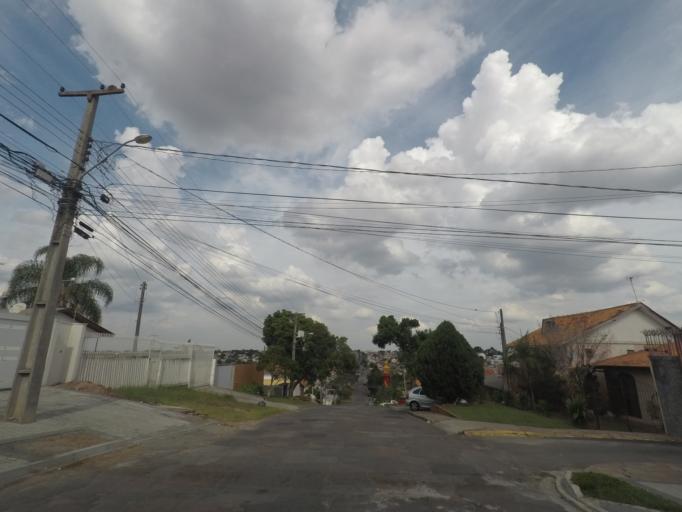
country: BR
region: Parana
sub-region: Curitiba
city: Curitiba
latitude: -25.4885
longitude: -49.2578
